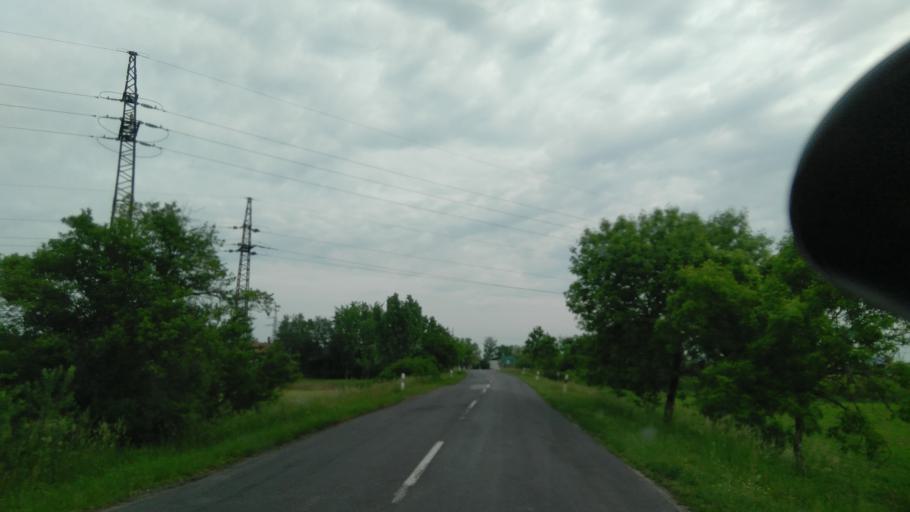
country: HU
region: Bekes
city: Szeghalom
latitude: 47.0093
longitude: 21.1802
